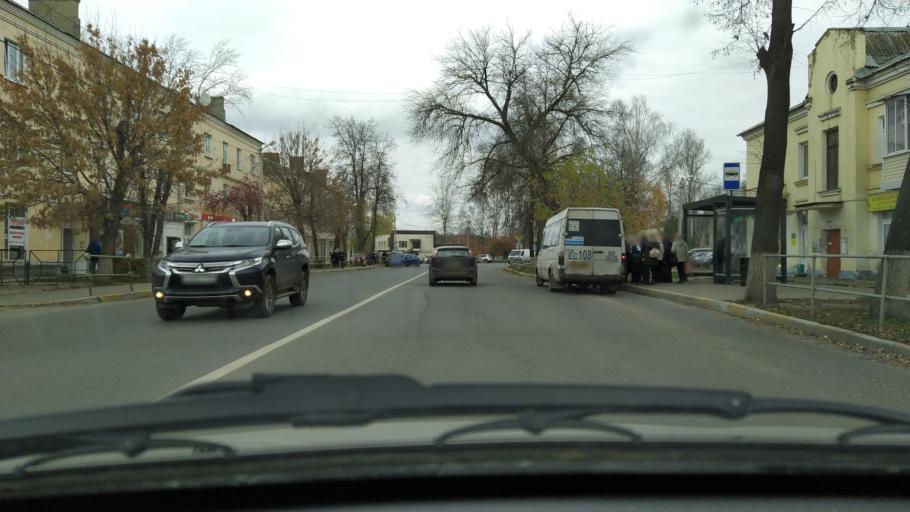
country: RU
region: Moskovskaya
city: Voskresensk
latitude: 55.3243
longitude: 38.6815
